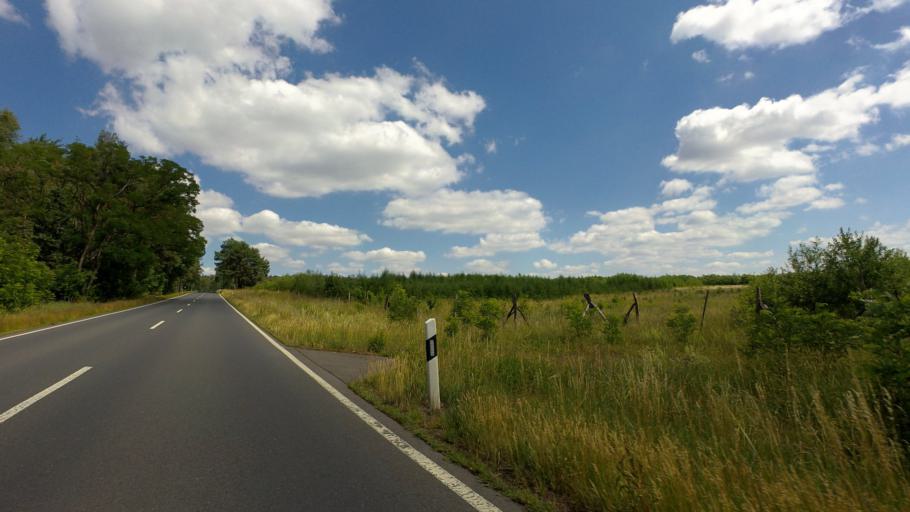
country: DE
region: Brandenburg
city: Sonnewalde
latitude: 51.7282
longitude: 13.6772
